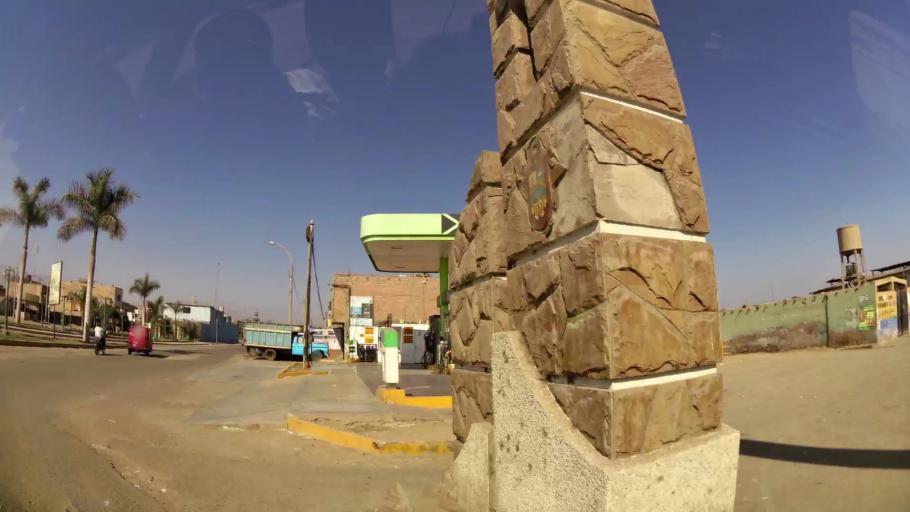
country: PE
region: Ica
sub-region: Provincia de Chincha
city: Chincha Alta
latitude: -13.4102
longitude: -76.1295
